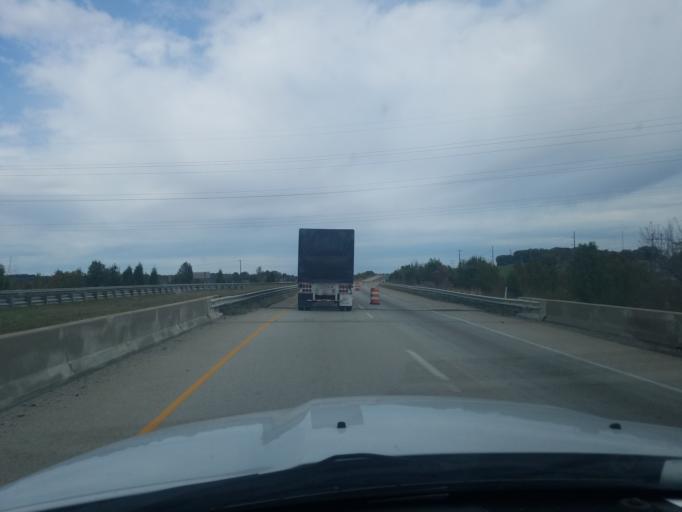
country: US
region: Indiana
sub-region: Vanderburgh County
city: Melody Hill
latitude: 38.1198
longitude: -87.4790
